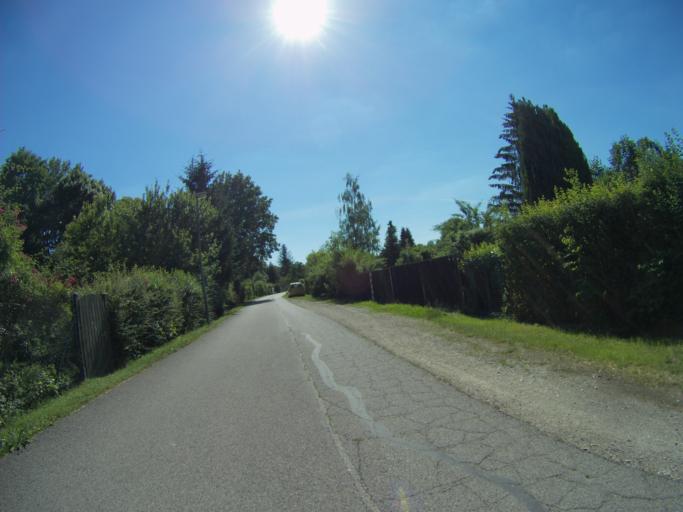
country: DE
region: Bavaria
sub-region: Upper Bavaria
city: Freising
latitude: 48.4023
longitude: 11.7557
